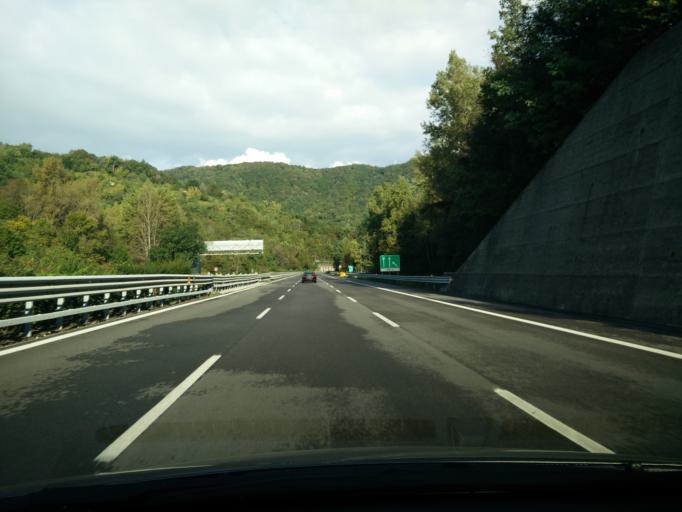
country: IT
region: Veneto
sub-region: Provincia di Treviso
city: Vittorio Veneto
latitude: 45.9801
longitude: 12.2802
